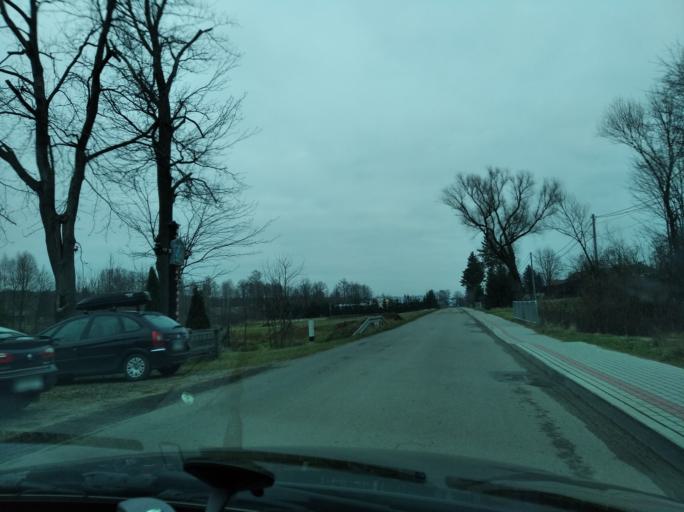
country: PL
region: Subcarpathian Voivodeship
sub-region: Powiat lancucki
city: Brzoza Stadnicka
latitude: 50.1953
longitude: 22.2692
